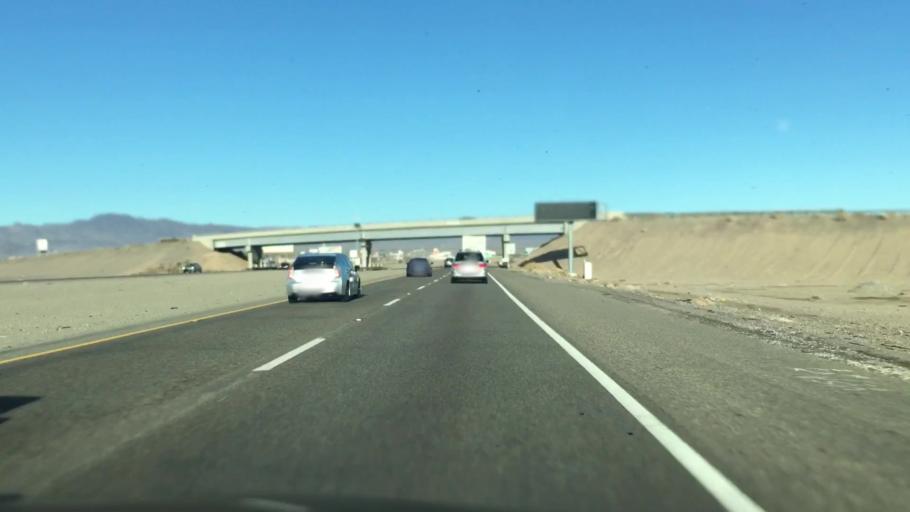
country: US
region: California
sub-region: San Bernardino County
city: Fort Irwin
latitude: 35.2556
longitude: -116.0851
